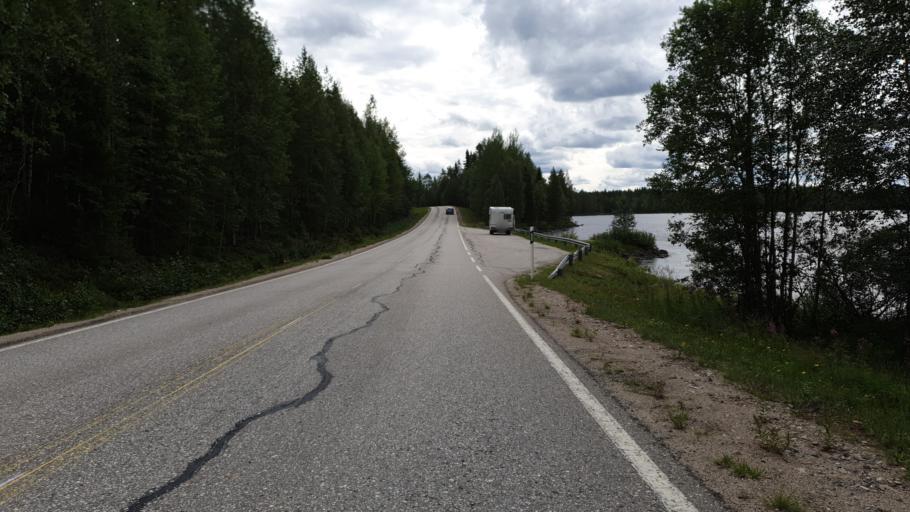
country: FI
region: Kainuu
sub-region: Kehys-Kainuu
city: Kuhmo
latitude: 64.4557
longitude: 29.7707
